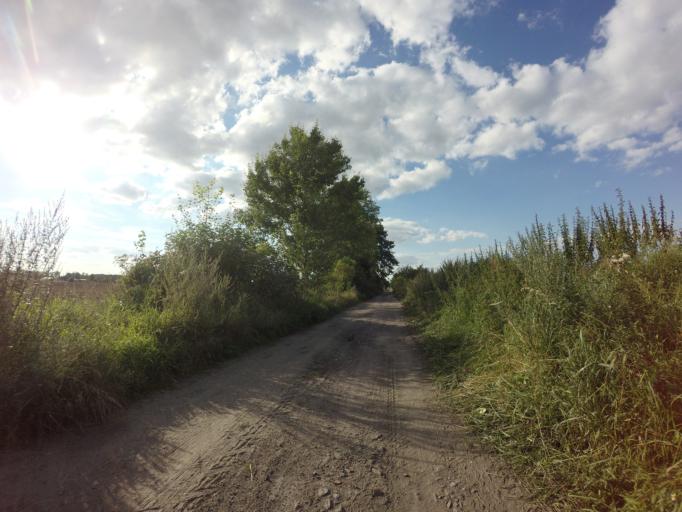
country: PL
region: West Pomeranian Voivodeship
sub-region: Powiat choszczenski
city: Choszczno
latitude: 53.2044
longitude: 15.4044
